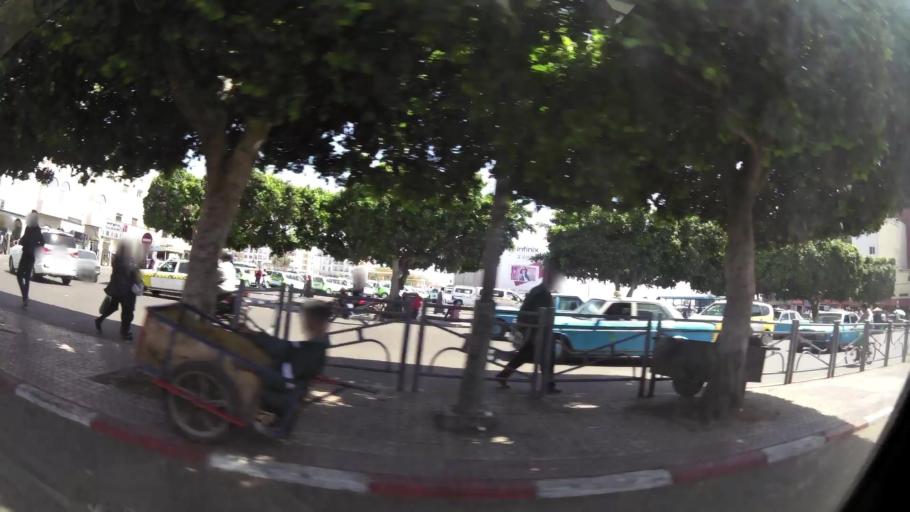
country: MA
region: Souss-Massa-Draa
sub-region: Inezgane-Ait Mellou
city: Inezgane
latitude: 30.3601
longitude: -9.5288
